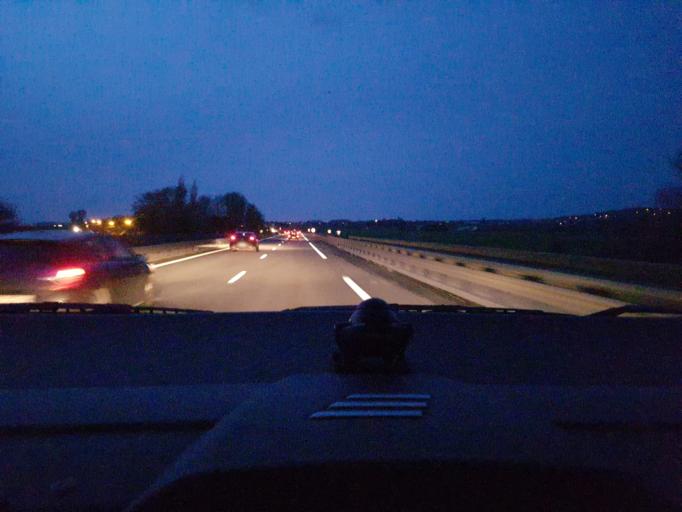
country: FR
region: Nord-Pas-de-Calais
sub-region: Departement du Nord
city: Meteren
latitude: 50.7439
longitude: 2.6778
